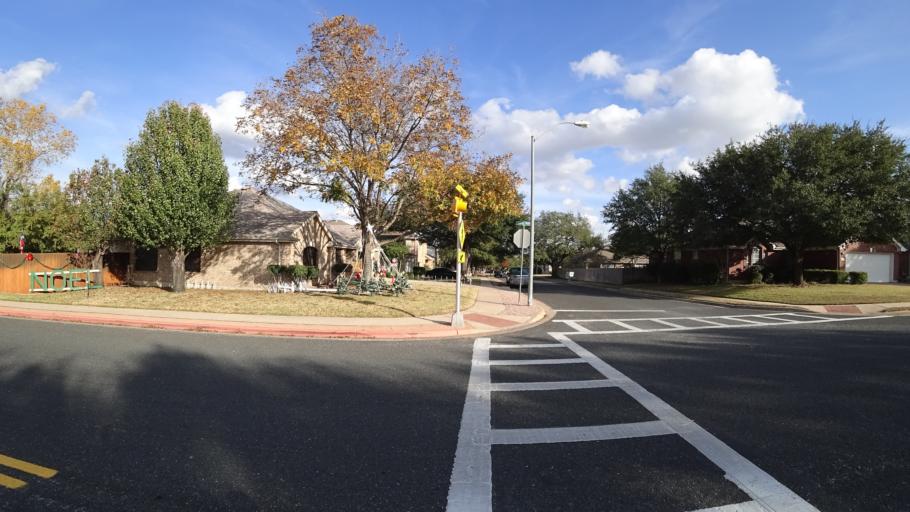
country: US
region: Texas
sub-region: Williamson County
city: Brushy Creek
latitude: 30.5051
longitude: -97.7306
